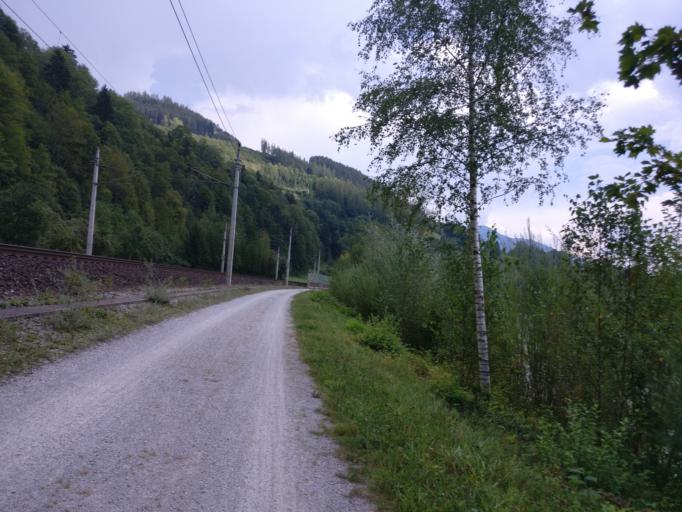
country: AT
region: Salzburg
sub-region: Politischer Bezirk Sankt Johann im Pongau
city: Pfarrwerfen
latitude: 47.4535
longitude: 13.2106
